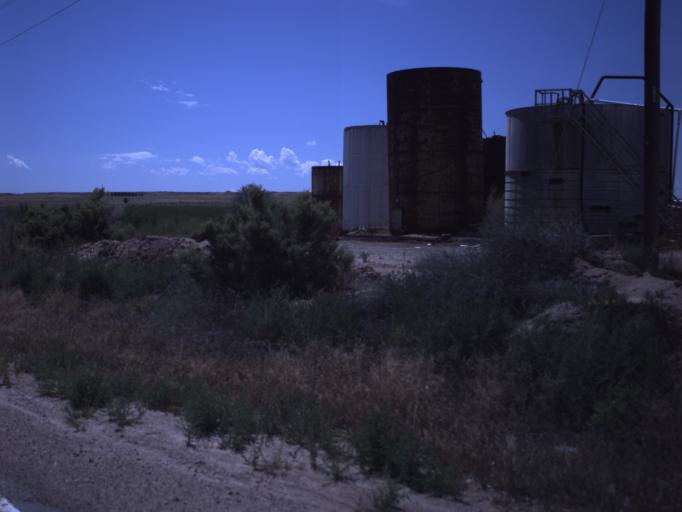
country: US
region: Utah
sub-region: Uintah County
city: Naples
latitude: 40.1400
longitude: -109.6640
